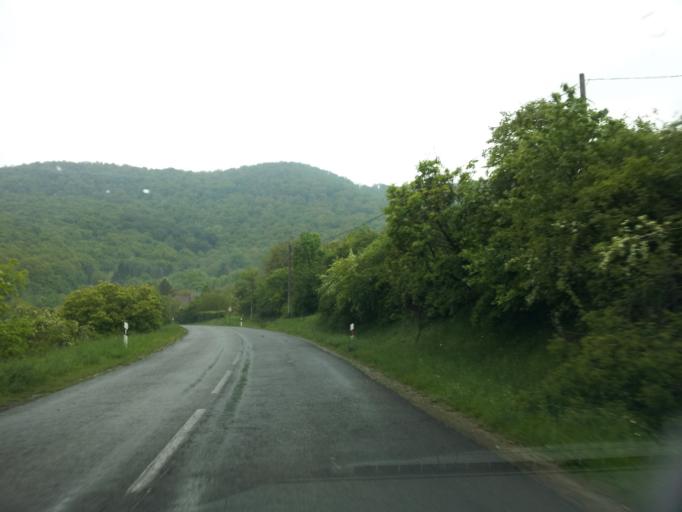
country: HU
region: Baranya
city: Hosszuheteny
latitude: 46.1688
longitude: 18.3435
